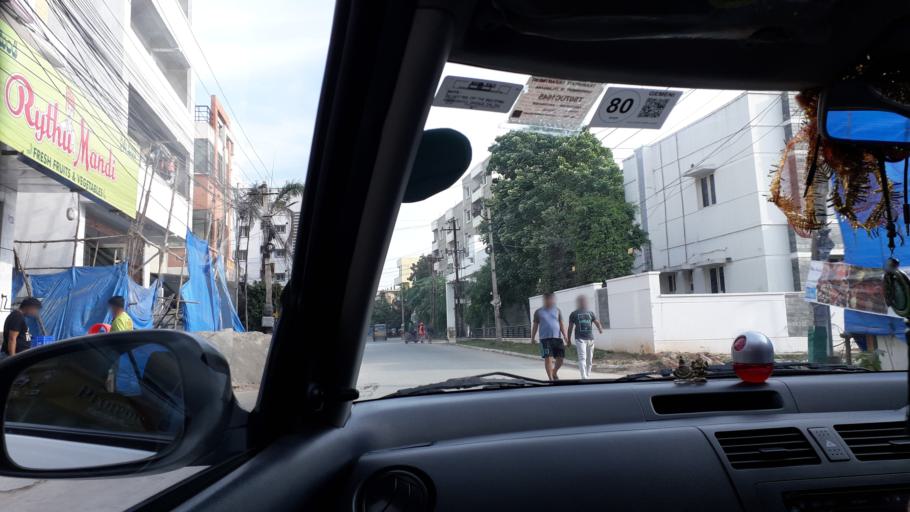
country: IN
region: Telangana
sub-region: Hyderabad
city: Hyderabad
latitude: 17.3975
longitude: 78.3777
